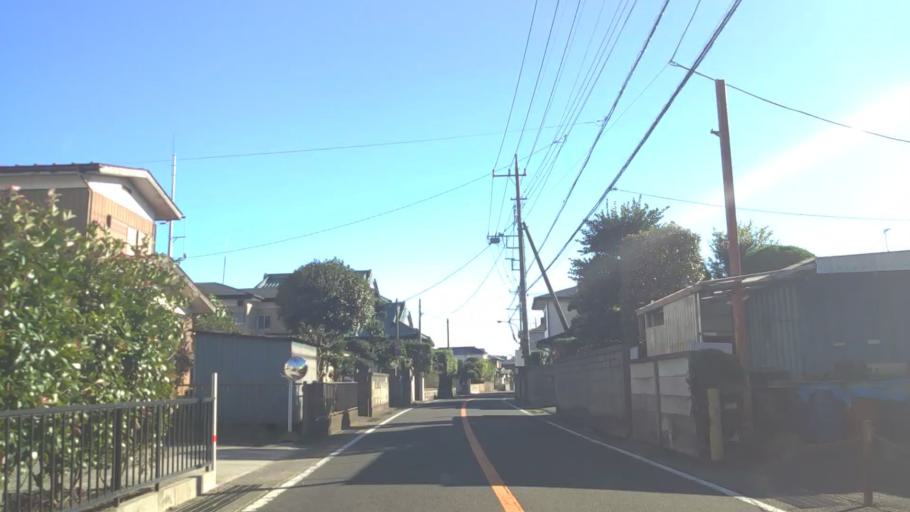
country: JP
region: Kanagawa
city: Atsugi
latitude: 35.4272
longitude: 139.3691
